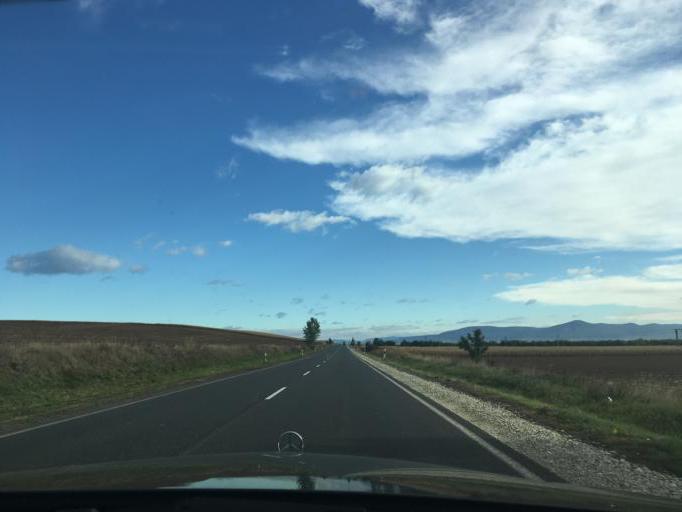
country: HU
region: Borsod-Abauj-Zemplen
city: Encs
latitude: 48.3451
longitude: 21.1187
